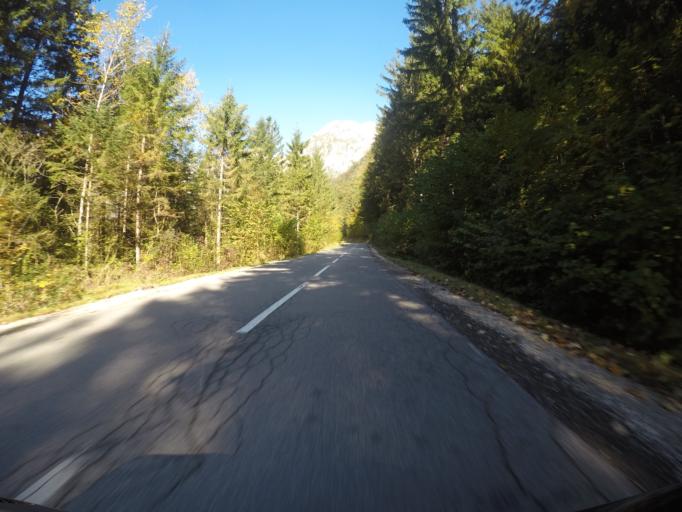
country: SI
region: Kamnik
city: Mekinje
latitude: 46.3230
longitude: 14.5936
